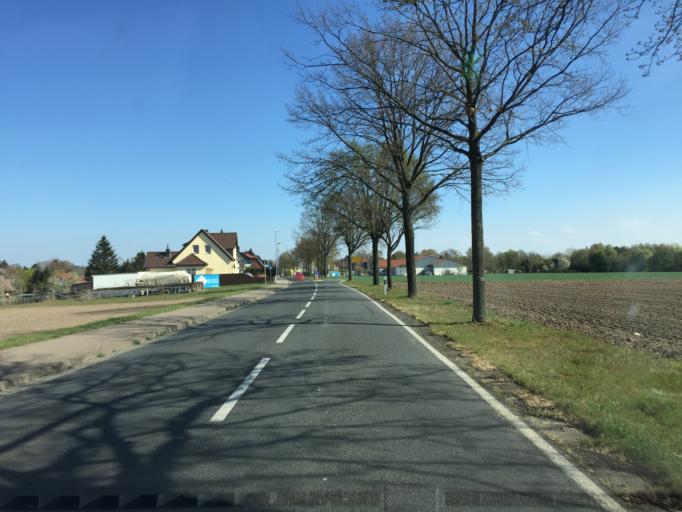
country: DE
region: Lower Saxony
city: Garbsen
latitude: 52.4027
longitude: 9.5485
